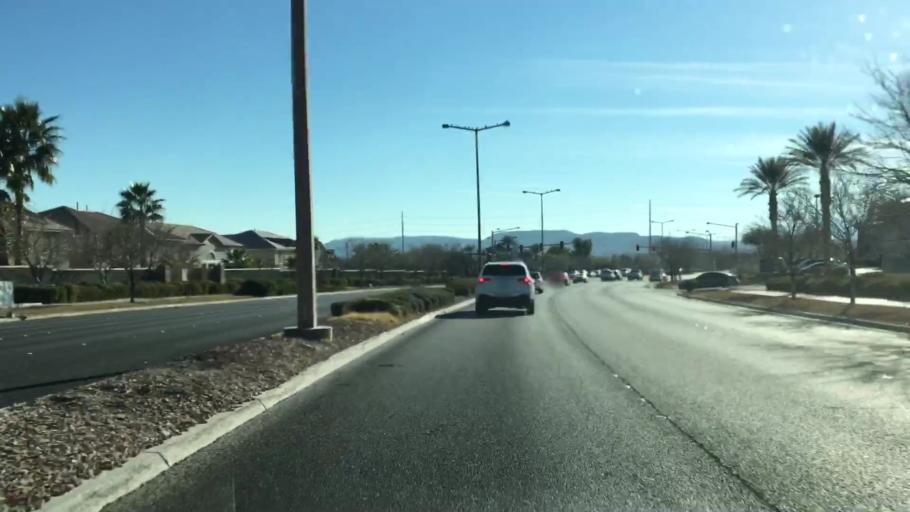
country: US
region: Nevada
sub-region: Clark County
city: Summerlin South
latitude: 36.1250
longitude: -115.3246
